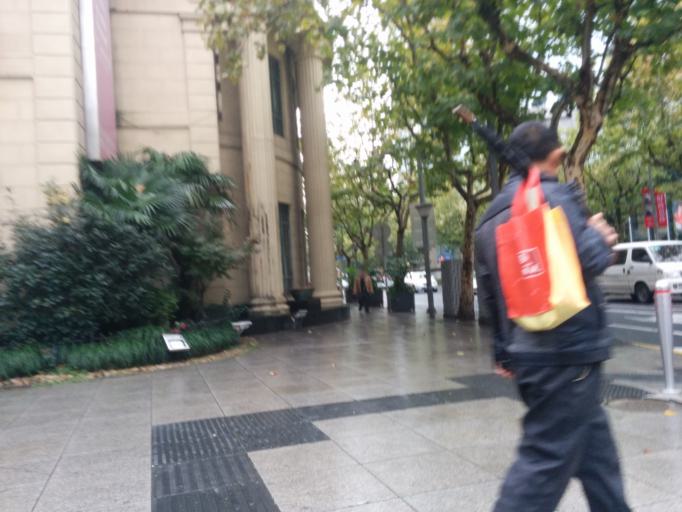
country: CN
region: Shanghai Shi
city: Shanghai
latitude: 31.2273
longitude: 121.4458
